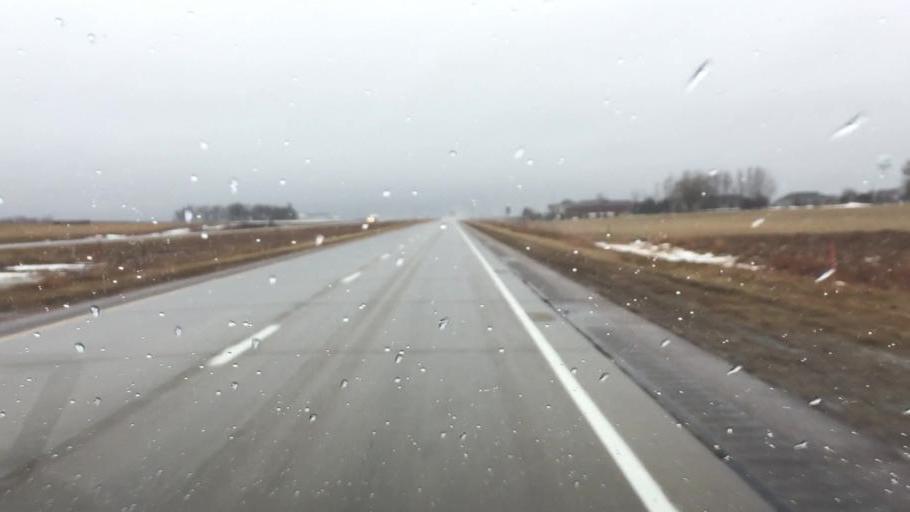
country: US
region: Iowa
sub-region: O'Brien County
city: Sheldon
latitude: 43.0766
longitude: -95.8988
